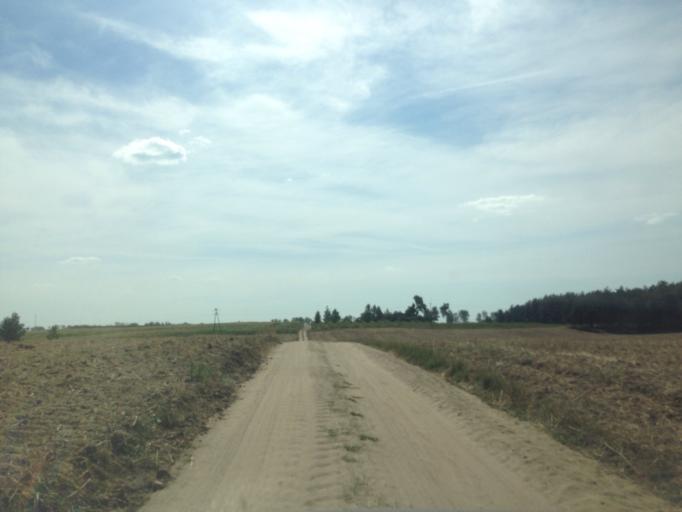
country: PL
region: Kujawsko-Pomorskie
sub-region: Powiat brodnicki
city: Gorzno
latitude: 53.2178
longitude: 19.6293
